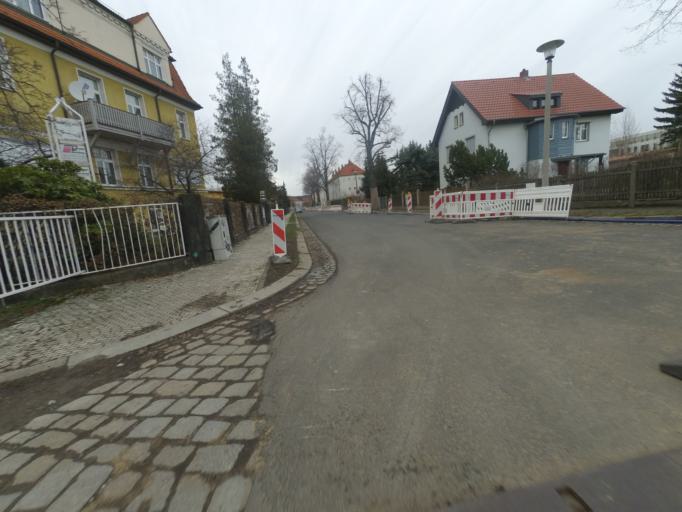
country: DE
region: Saxony
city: Heidenau
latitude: 51.0060
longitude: 13.8236
